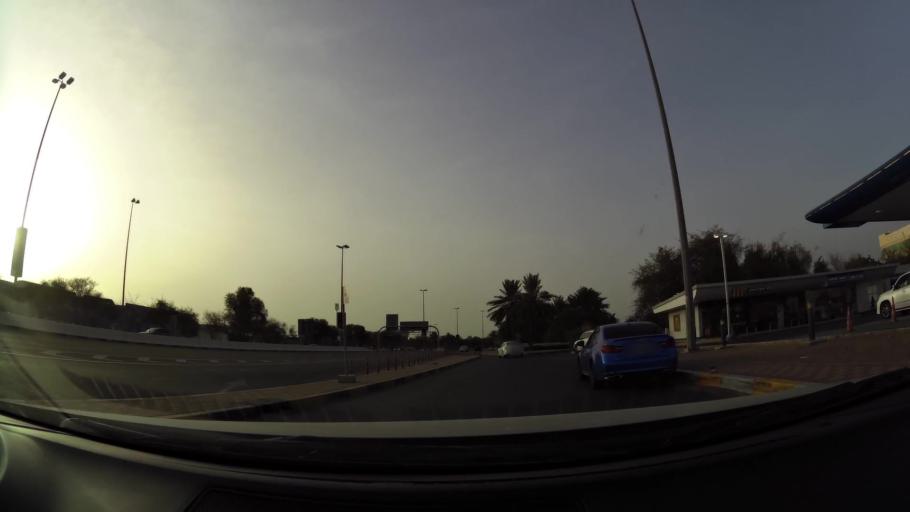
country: AE
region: Abu Dhabi
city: Al Ain
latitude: 24.2453
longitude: 55.7199
